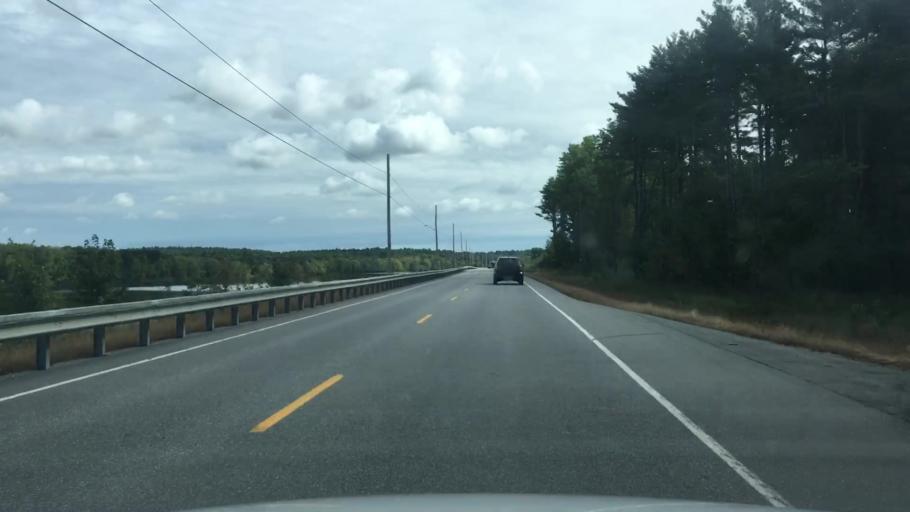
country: US
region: Maine
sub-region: Androscoggin County
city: Lisbon
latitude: 44.0019
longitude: -70.1546
